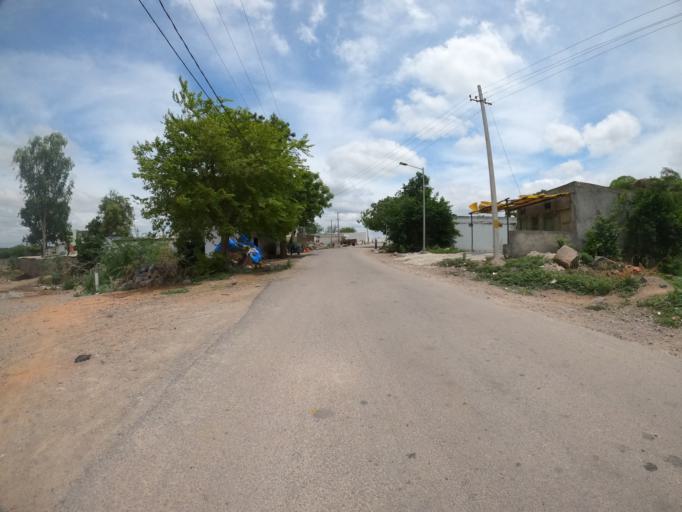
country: IN
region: Telangana
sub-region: Hyderabad
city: Hyderabad
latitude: 17.2980
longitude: 78.3786
